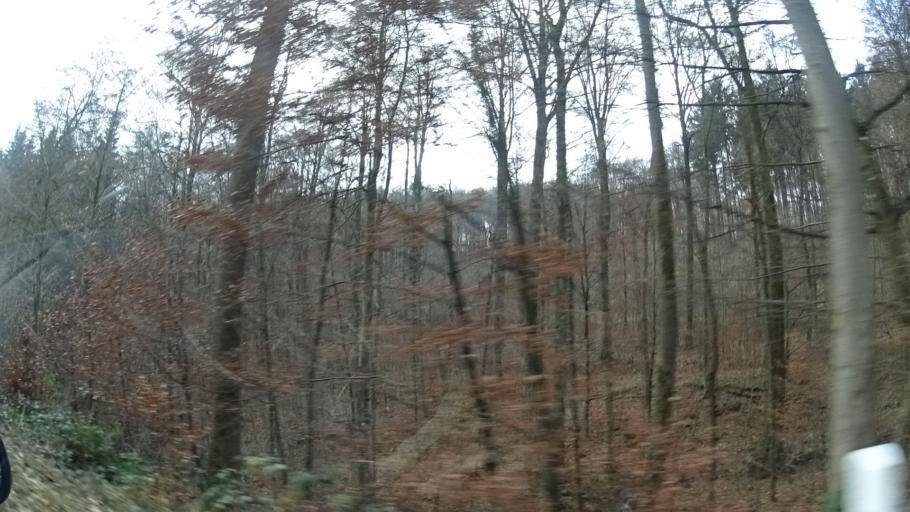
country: DE
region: Baden-Wuerttemberg
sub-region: Karlsruhe Region
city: Gaiberg
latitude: 49.3833
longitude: 8.7609
